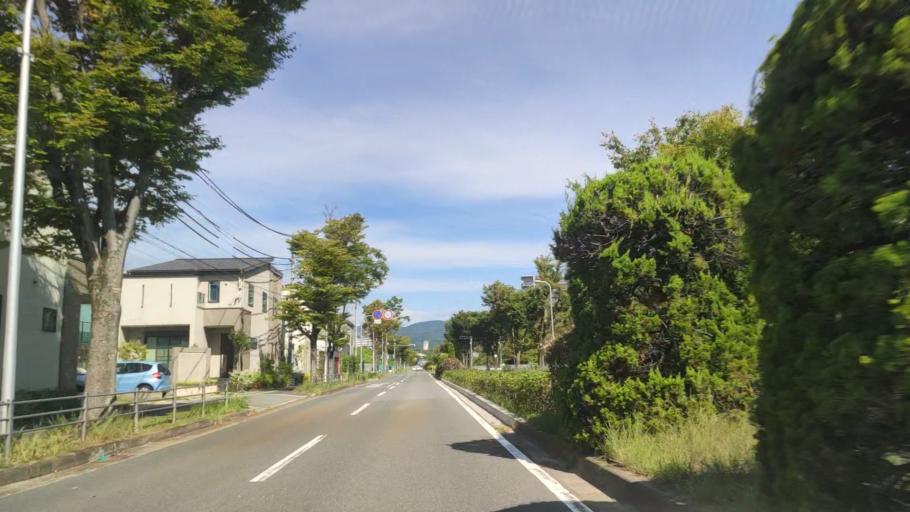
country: JP
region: Osaka
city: Mino
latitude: 34.8149
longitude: 135.5140
